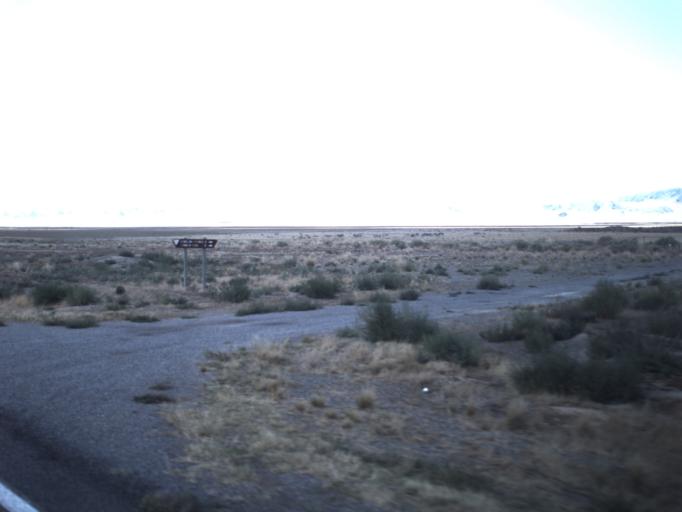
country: US
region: Utah
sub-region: Millard County
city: Delta
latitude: 38.9821
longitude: -112.7947
